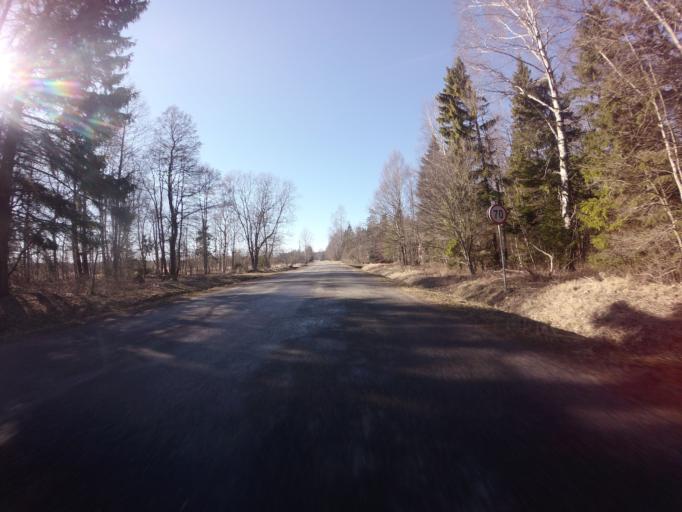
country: EE
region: Saare
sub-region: Kuressaare linn
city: Kuressaare
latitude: 58.5741
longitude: 22.6575
